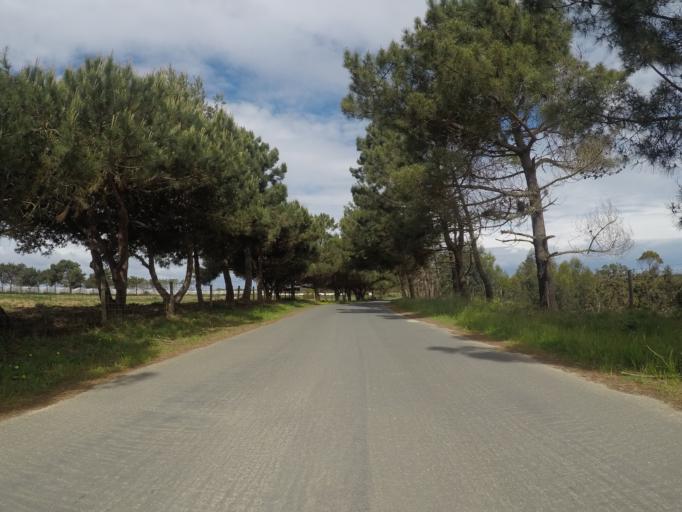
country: PT
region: Beja
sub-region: Odemira
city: Sao Teotonio
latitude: 37.4954
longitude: -8.7879
